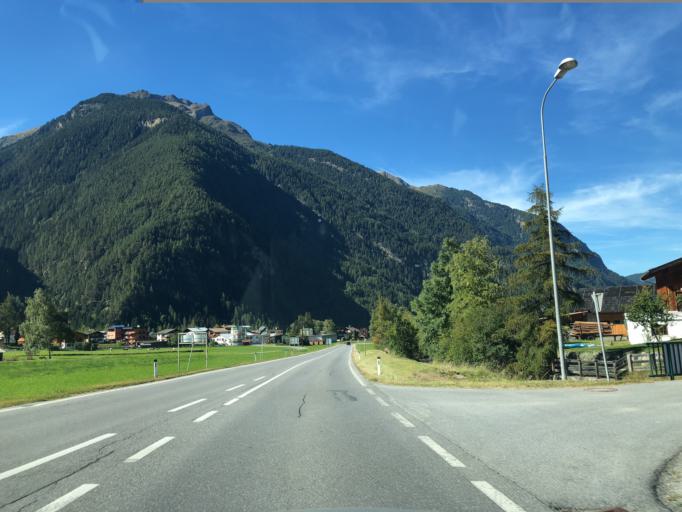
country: AT
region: Tyrol
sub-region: Politischer Bezirk Imst
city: Umhausen
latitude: 47.1410
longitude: 10.9215
